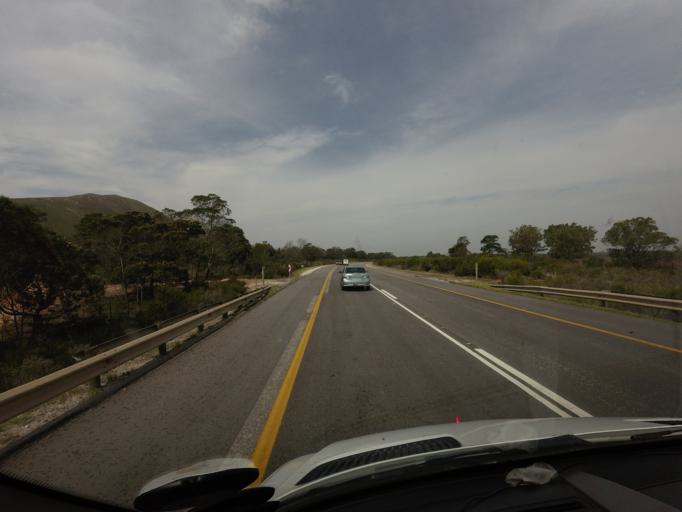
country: ZA
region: Eastern Cape
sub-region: Cacadu District Municipality
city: Kruisfontein
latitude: -33.9940
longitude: 24.7315
